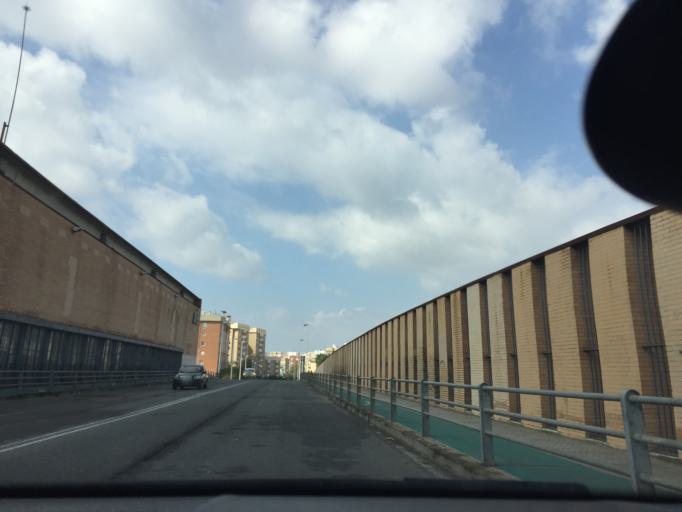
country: ES
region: Andalusia
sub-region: Provincia de Sevilla
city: Sevilla
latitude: 37.3941
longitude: -5.9720
